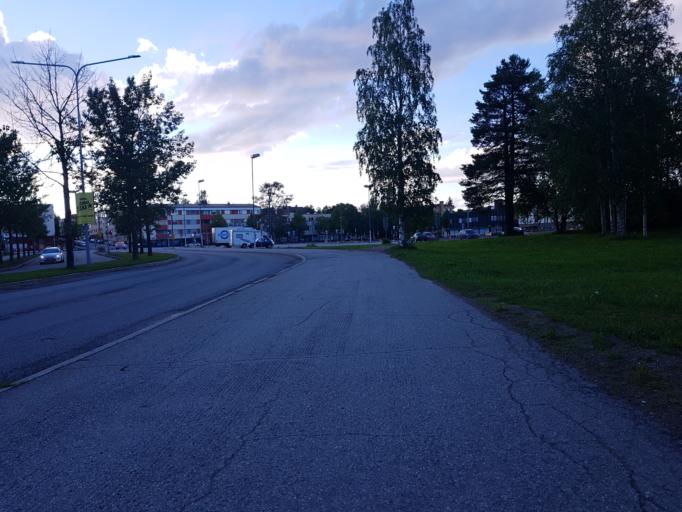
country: FI
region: Kainuu
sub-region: Kajaani
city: Kajaani
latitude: 64.2210
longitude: 27.7293
